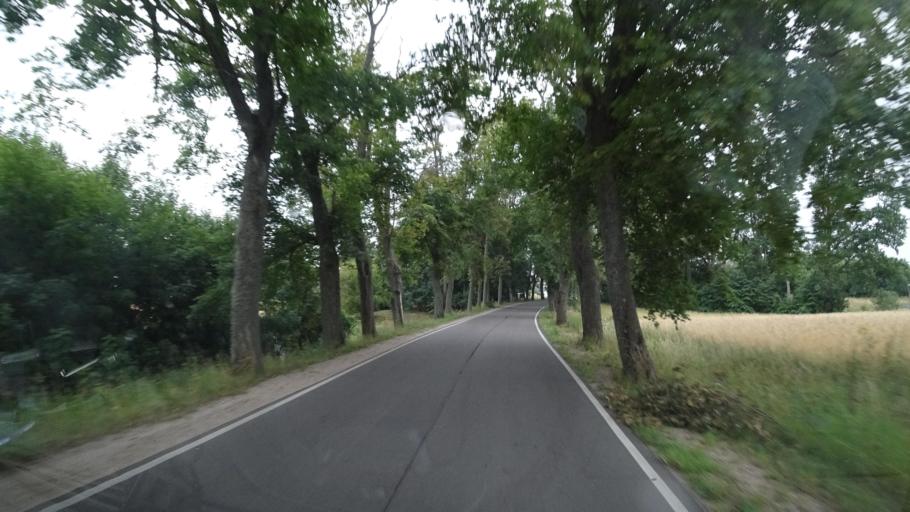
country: PL
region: Warmian-Masurian Voivodeship
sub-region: Powiat mragowski
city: Mikolajki
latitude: 53.8537
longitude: 21.6145
